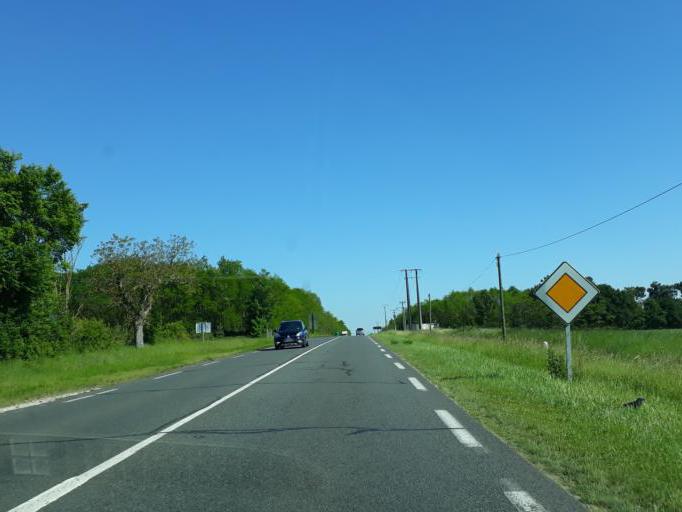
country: FR
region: Centre
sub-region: Departement du Loiret
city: Briare
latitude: 47.6204
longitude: 2.7605
